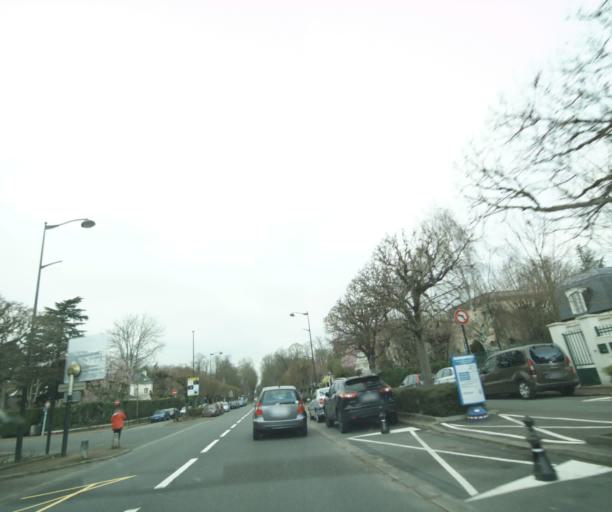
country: FR
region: Ile-de-France
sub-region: Departement des Yvelines
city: Saint-Germain-en-Laye
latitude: 48.9039
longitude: 2.0836
